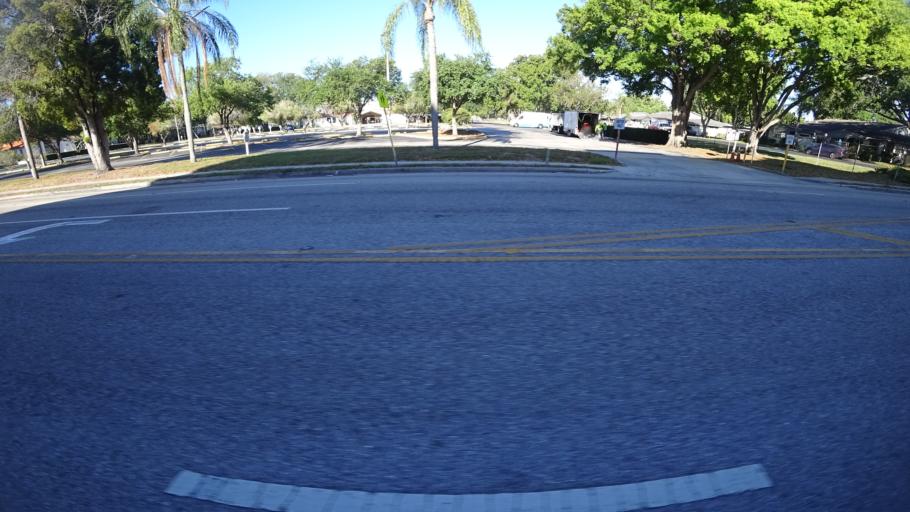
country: US
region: Florida
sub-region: Manatee County
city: South Bradenton
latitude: 27.4742
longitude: -82.5877
